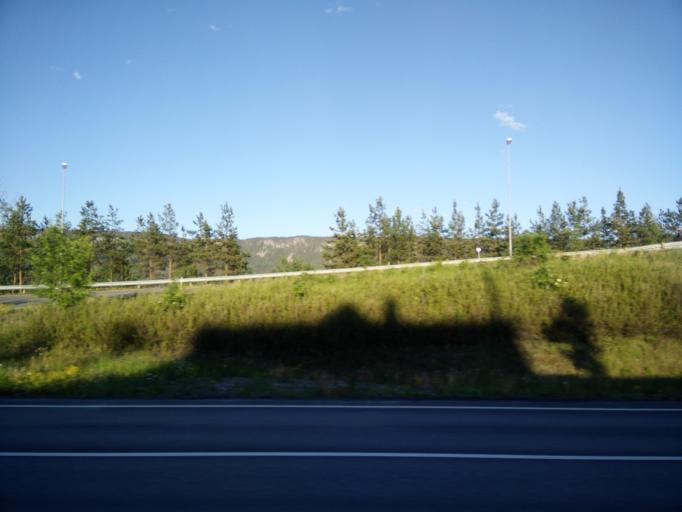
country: NO
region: Buskerud
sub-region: Hole
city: Vik
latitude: 60.0911
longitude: 10.2903
